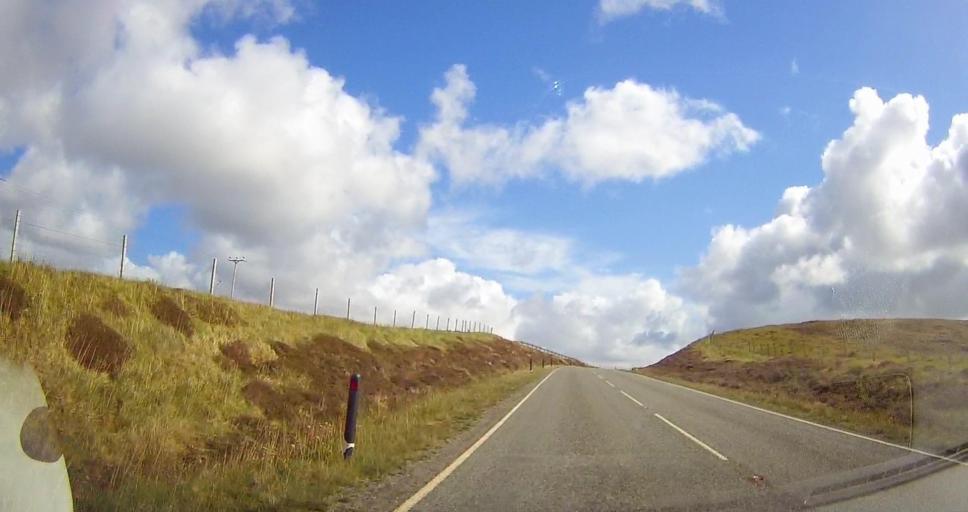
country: GB
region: Scotland
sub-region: Shetland Islands
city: Lerwick
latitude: 60.4568
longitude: -1.3977
